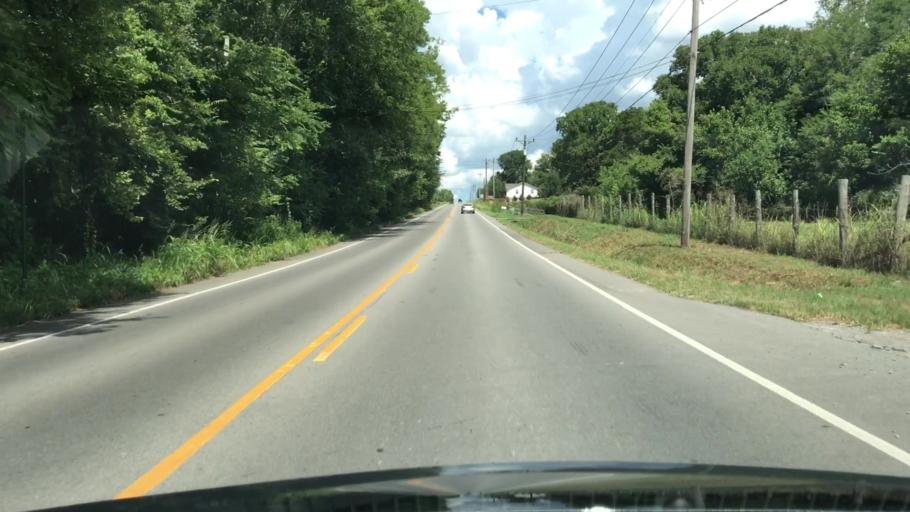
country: US
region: Tennessee
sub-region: Williamson County
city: Nolensville
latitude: 35.8611
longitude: -86.6587
